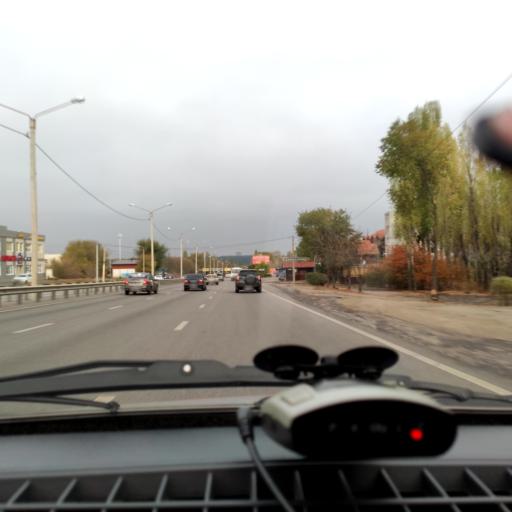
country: RU
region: Voronezj
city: Voronezh
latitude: 51.6585
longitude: 39.1337
